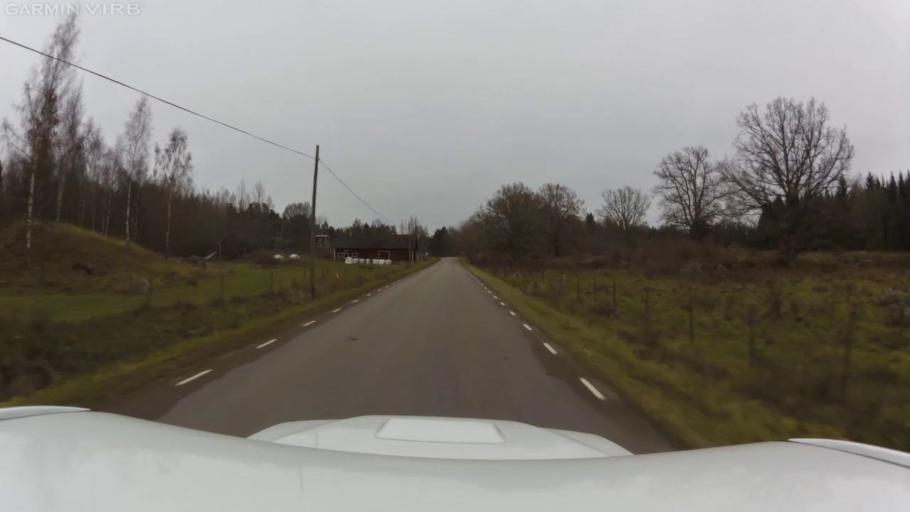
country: SE
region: OEstergoetland
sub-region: Linkopings Kommun
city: Vikingstad
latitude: 58.2543
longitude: 15.3836
